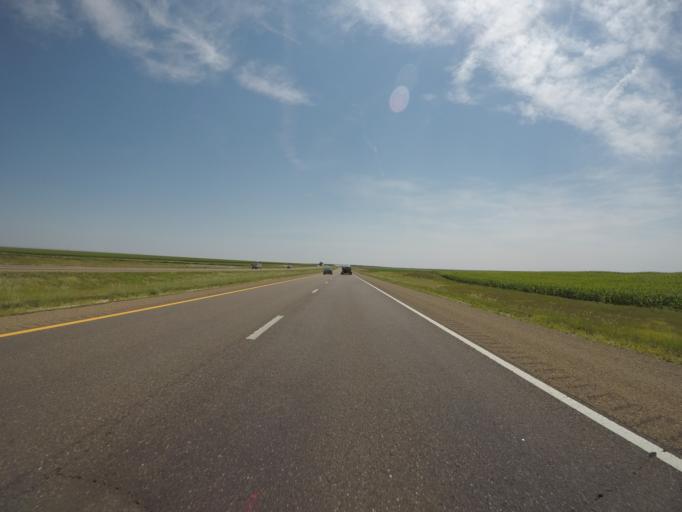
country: US
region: Kansas
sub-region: Sherman County
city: Goodland
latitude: 39.3300
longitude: -101.4803
